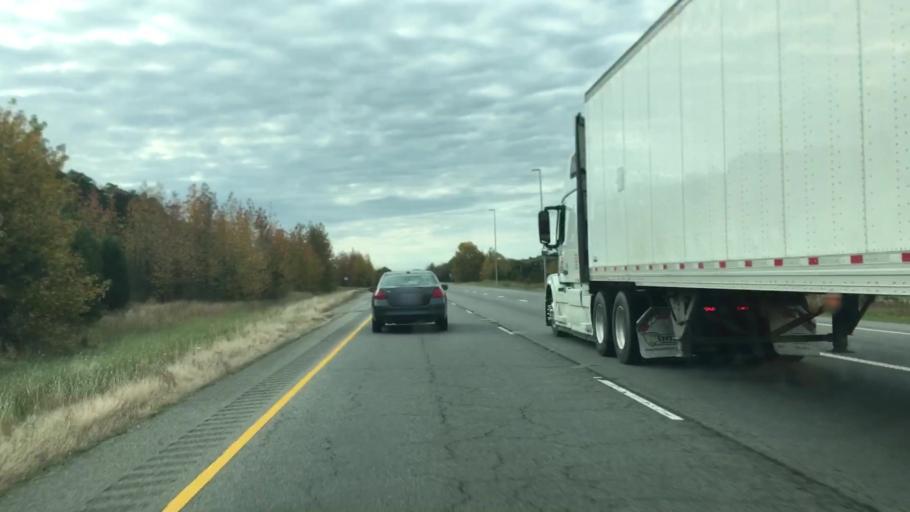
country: US
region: Arkansas
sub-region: Faulkner County
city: Conway
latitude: 35.1195
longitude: -92.4656
